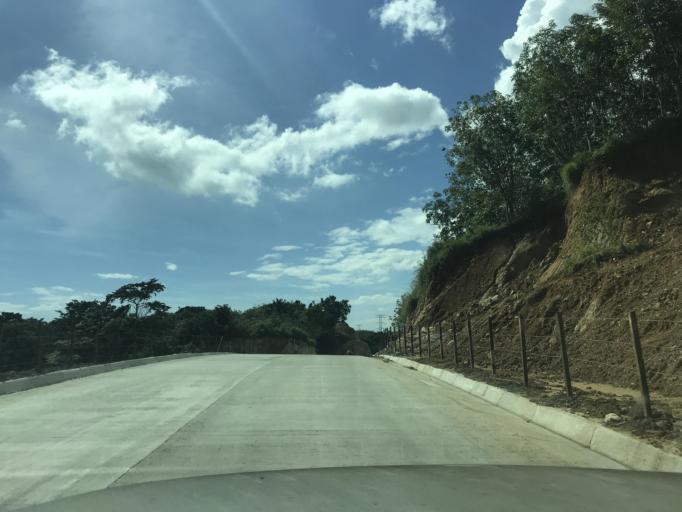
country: GT
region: Izabal
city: Morales
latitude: 15.6434
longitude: -89.0299
